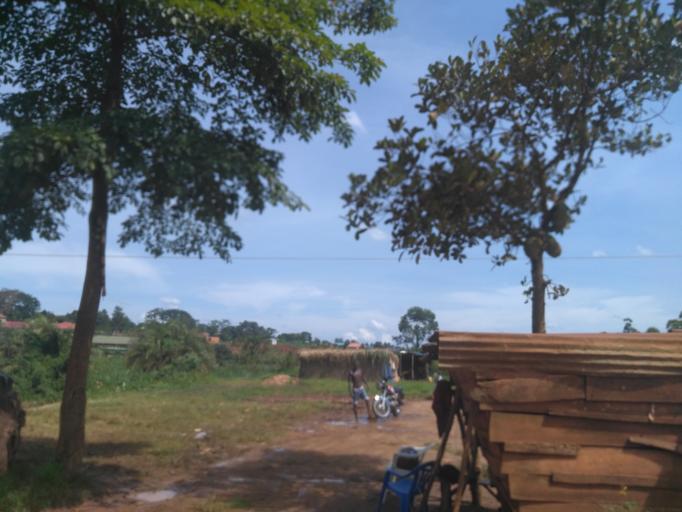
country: UG
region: Central Region
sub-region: Wakiso District
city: Kireka
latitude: 0.4409
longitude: 32.5941
